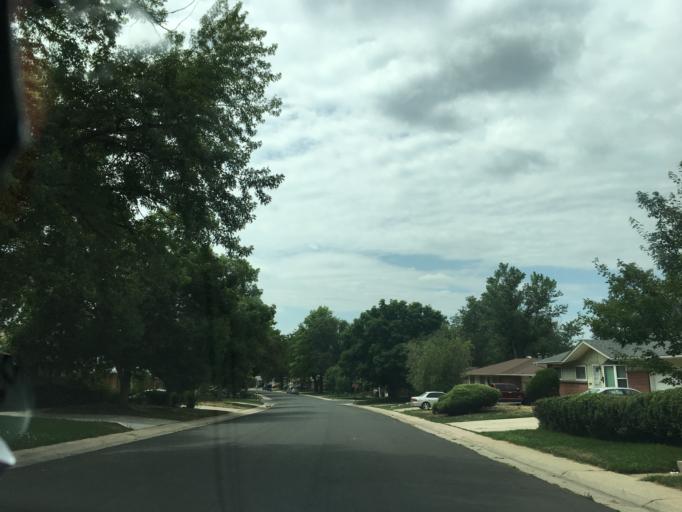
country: US
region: Colorado
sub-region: Arapahoe County
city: Sheridan
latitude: 39.6611
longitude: -105.0482
